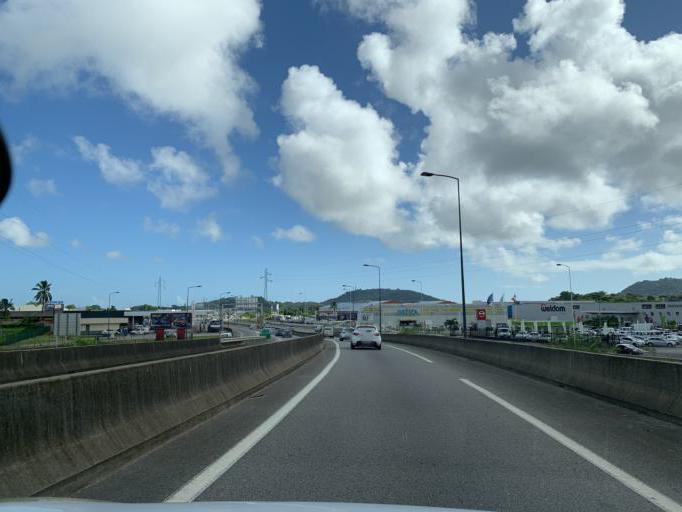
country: GF
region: Guyane
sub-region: Guyane
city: Cayenne
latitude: 4.8918
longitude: -52.3327
